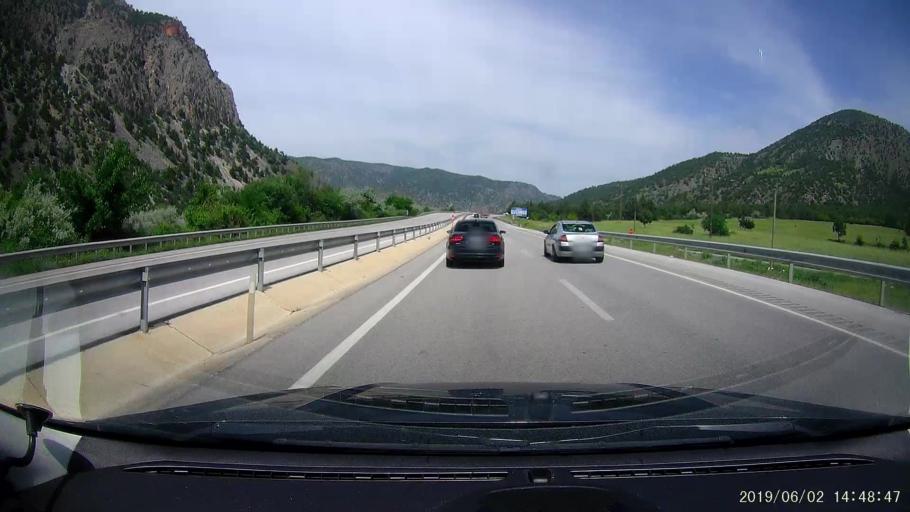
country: TR
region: Corum
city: Hacihamza
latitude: 41.0631
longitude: 34.4884
